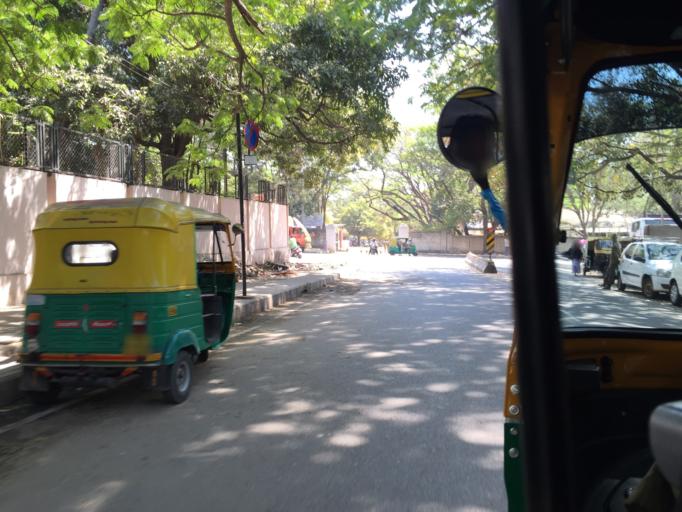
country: IN
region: Karnataka
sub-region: Bangalore Urban
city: Bangalore
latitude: 12.9695
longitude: 77.6152
